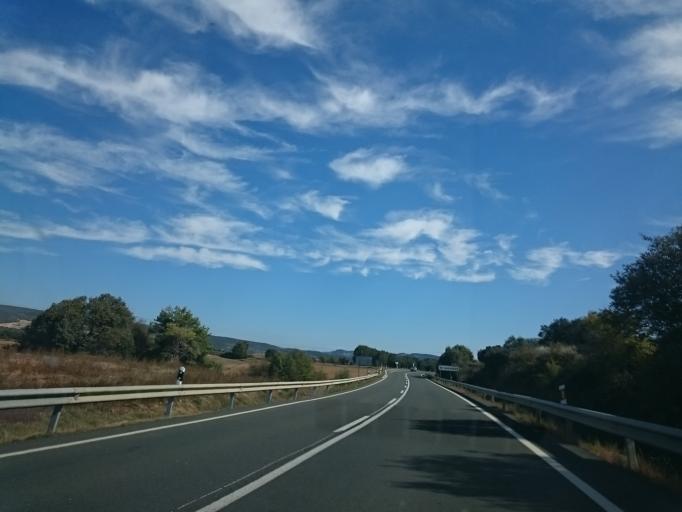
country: ES
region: Aragon
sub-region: Provincia de Huesca
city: Benavarri / Benabarre
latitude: 42.1131
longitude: 0.5256
